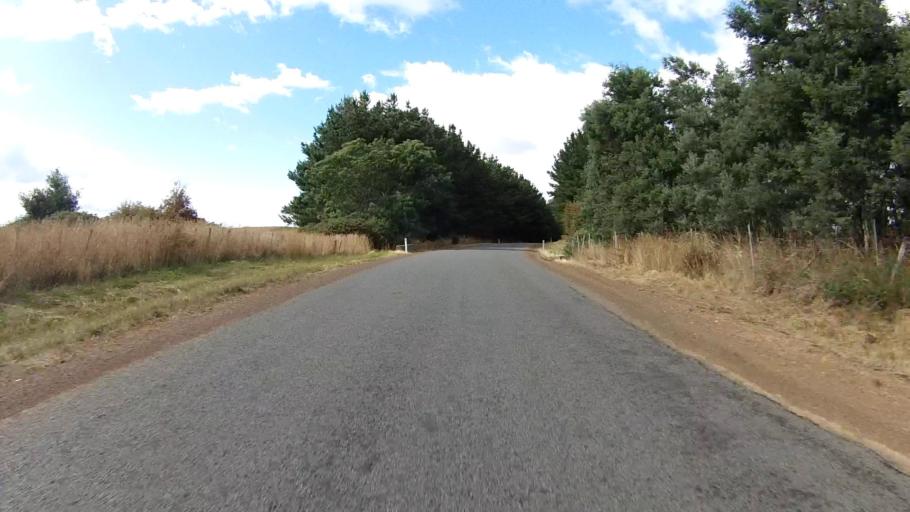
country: AU
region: Tasmania
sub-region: Northern Midlands
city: Evandale
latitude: -41.6932
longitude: 147.3658
